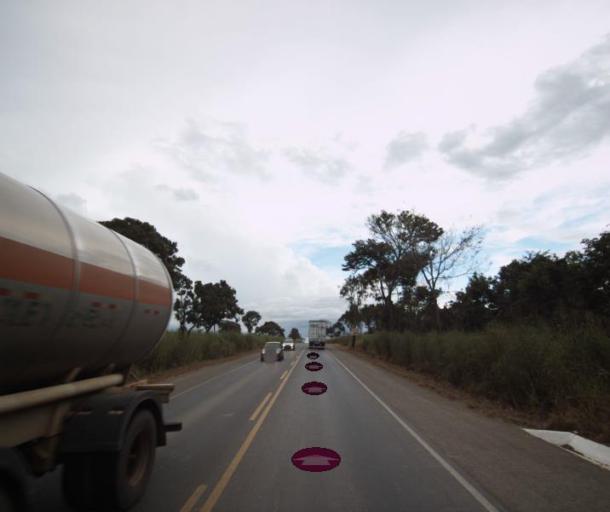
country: BR
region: Goias
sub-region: Itapaci
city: Itapaci
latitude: -14.9085
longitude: -49.3529
